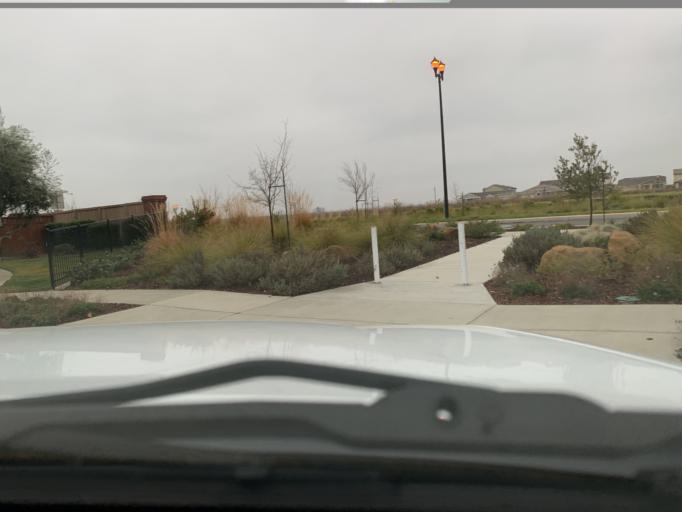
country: US
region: California
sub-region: Yolo County
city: Woodland
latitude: 38.6454
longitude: -121.7441
